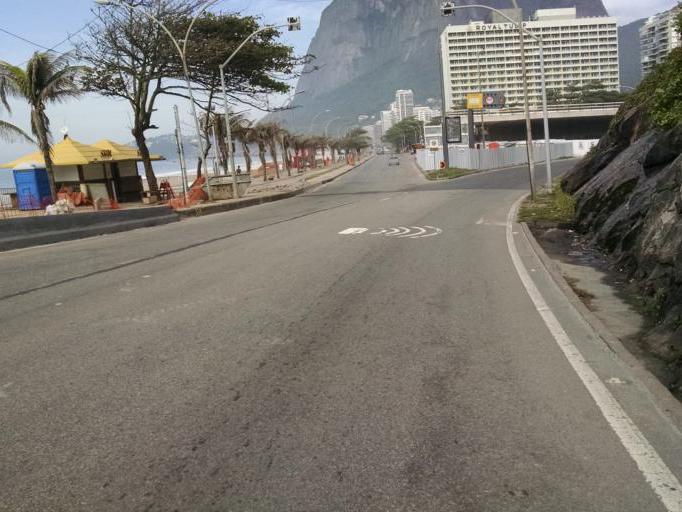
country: BR
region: Rio de Janeiro
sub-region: Rio De Janeiro
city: Rio de Janeiro
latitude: -22.9984
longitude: -43.2554
